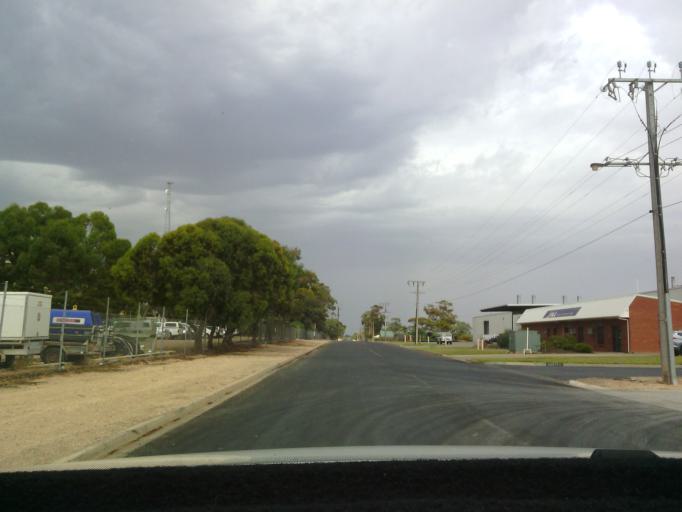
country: AU
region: South Australia
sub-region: Berri and Barmera
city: Berri
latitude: -34.2715
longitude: 140.6003
